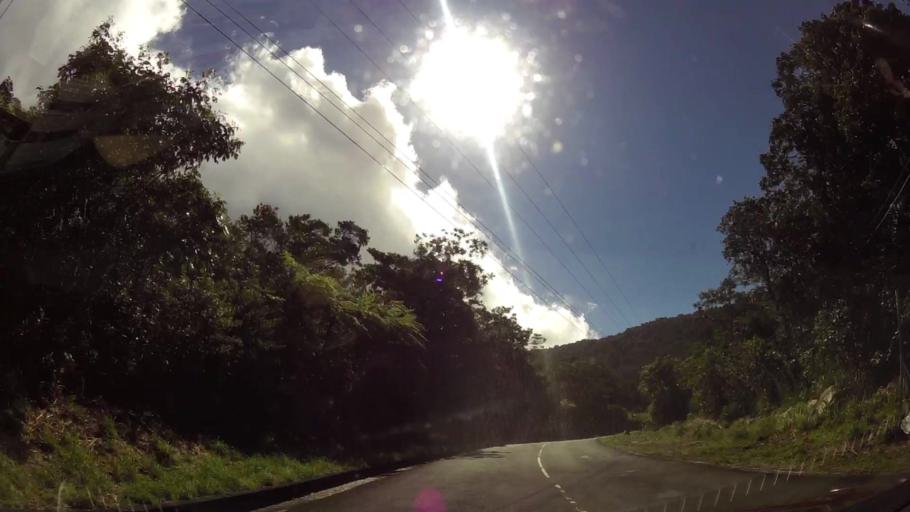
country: DM
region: Saint Paul
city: Pont Casse
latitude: 15.3765
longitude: -61.3439
